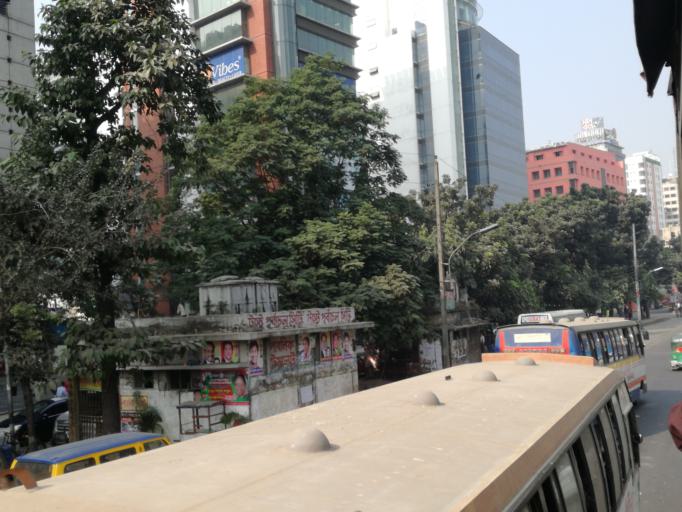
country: BD
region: Dhaka
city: Tungi
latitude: 23.8616
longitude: 90.4000
